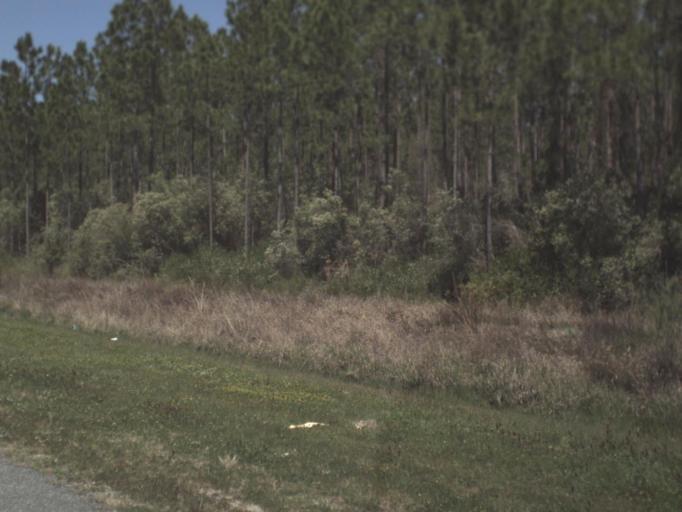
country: US
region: Florida
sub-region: Gulf County
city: Port Saint Joe
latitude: 29.8852
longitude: -85.3451
